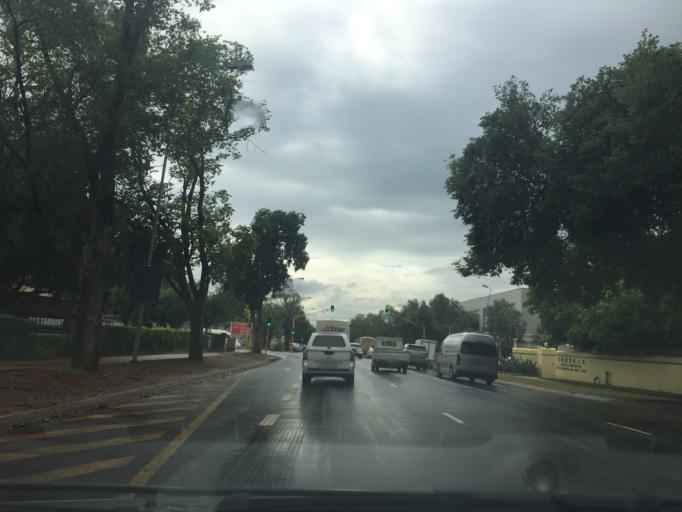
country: ZA
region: Gauteng
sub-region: City of Tshwane Metropolitan Municipality
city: Pretoria
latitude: -25.7461
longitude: 28.2366
